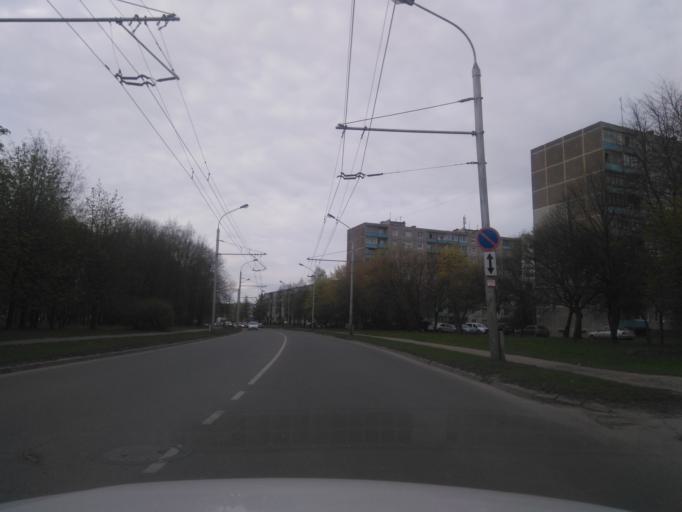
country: LT
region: Kauno apskritis
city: Dainava (Kaunas)
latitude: 54.9181
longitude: 23.9719
